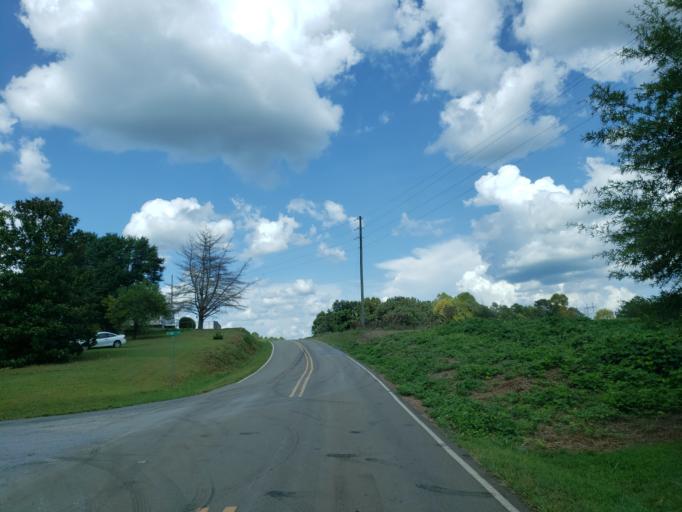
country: US
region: Georgia
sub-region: Pickens County
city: Jasper
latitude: 34.4293
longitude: -84.4372
